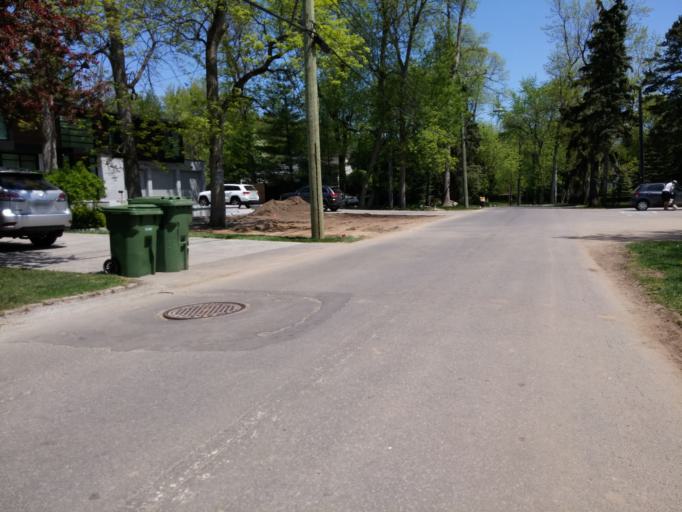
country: CA
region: Quebec
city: Beaconsfield
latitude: 45.4171
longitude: -73.8795
